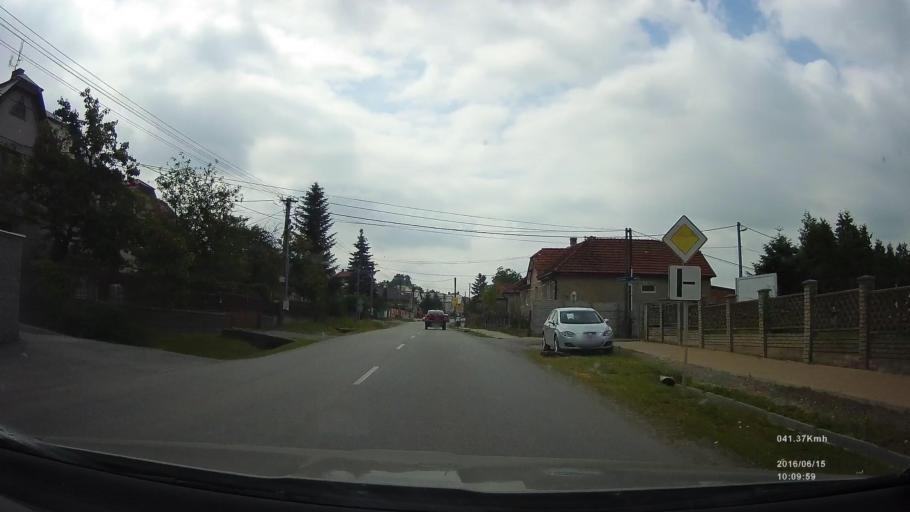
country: SK
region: Kosicky
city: Kosice
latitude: 48.7557
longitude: 21.3422
